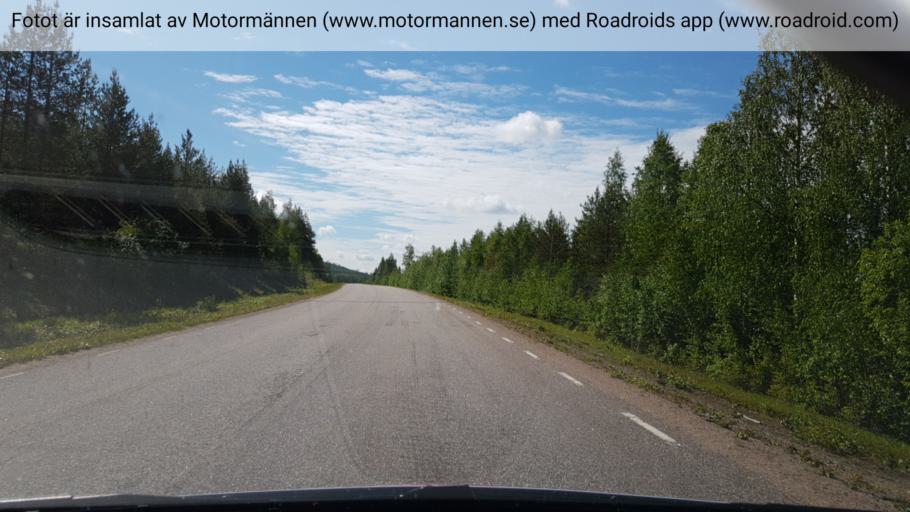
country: FI
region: Lapland
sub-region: Torniolaakso
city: Pello
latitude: 66.6918
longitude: 23.8401
